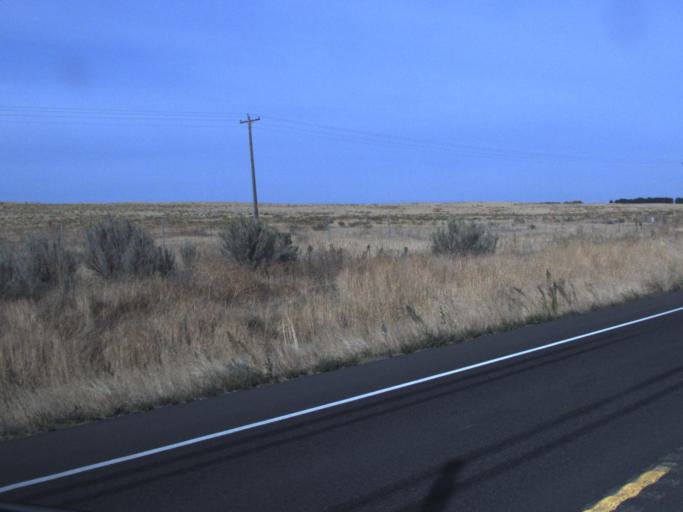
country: US
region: Oregon
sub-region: Morrow County
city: Irrigon
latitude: 45.9439
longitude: -119.5245
